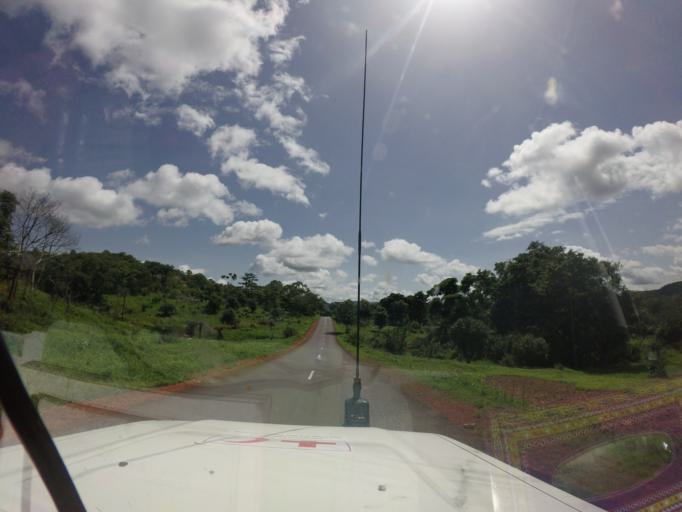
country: GN
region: Mamou
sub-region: Mamou Prefecture
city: Mamou
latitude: 10.1780
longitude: -11.8136
